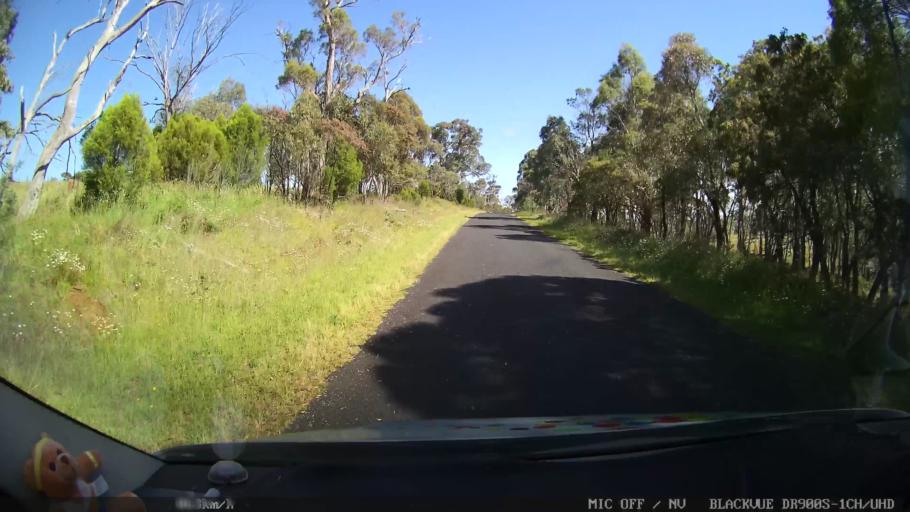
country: AU
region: New South Wales
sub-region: Guyra
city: Guyra
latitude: -30.0634
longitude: 151.6656
